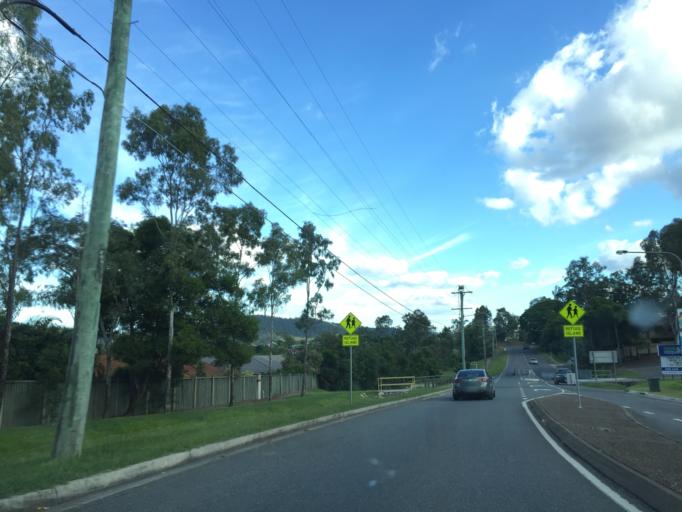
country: AU
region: Queensland
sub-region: Moreton Bay
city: Ferny Hills
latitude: -27.4304
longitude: 152.9436
